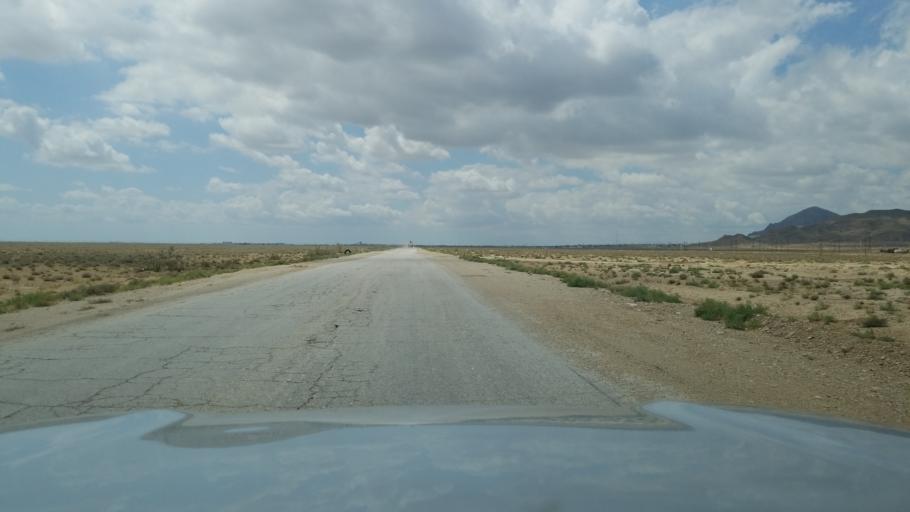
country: TM
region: Balkan
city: Balkanabat
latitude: 39.4817
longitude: 54.4464
